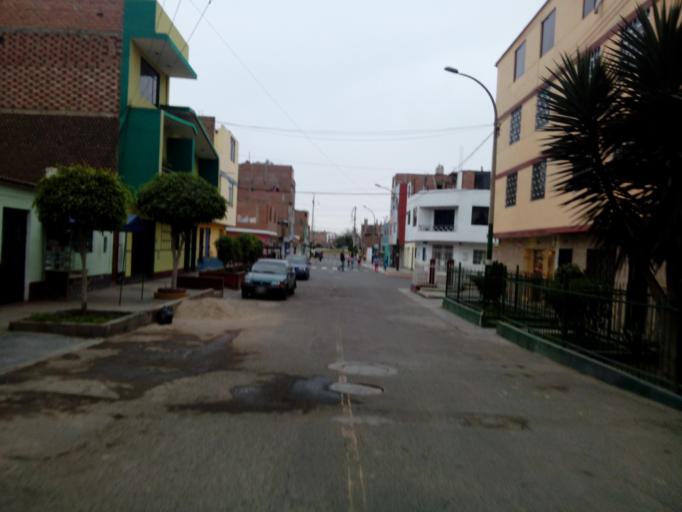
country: PE
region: Callao
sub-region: Callao
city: Callao
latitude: -12.0391
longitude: -77.0860
